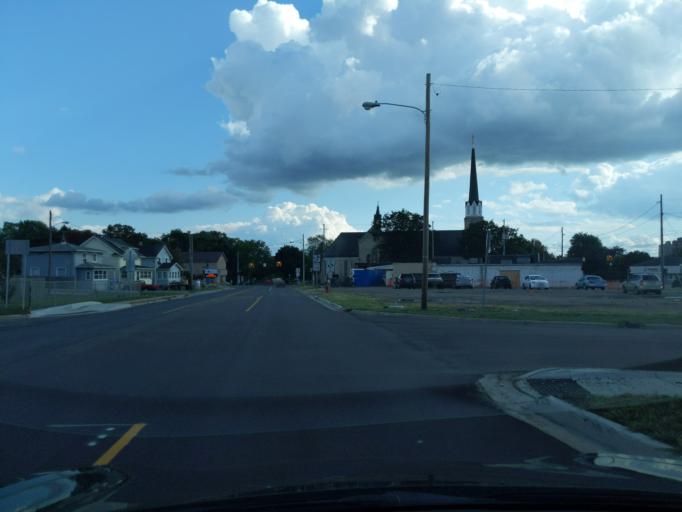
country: US
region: Michigan
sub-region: Jackson County
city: Jackson
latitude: 42.2559
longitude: -84.4035
